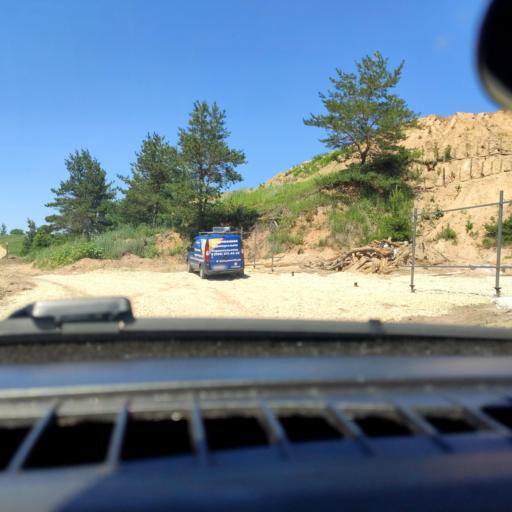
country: RU
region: Voronezj
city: Podgornoye
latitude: 51.7980
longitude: 39.1359
